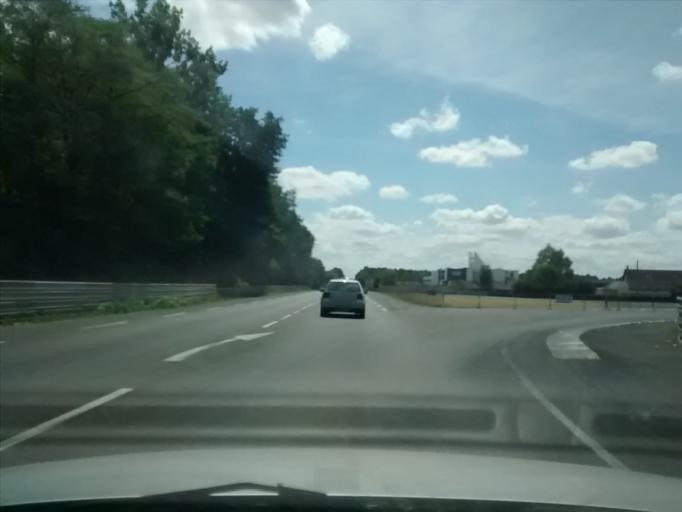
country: FR
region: Pays de la Loire
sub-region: Departement de la Sarthe
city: Ruaudin
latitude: 47.9452
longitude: 0.2331
